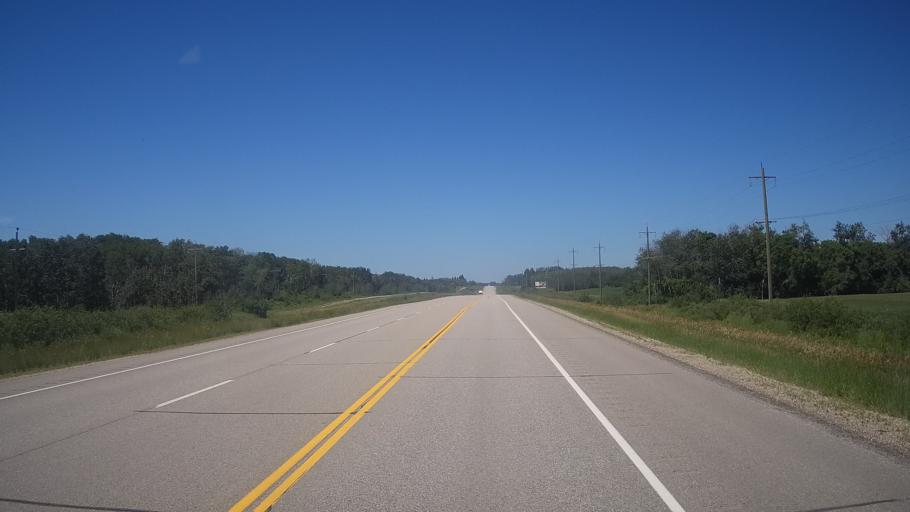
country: CA
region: Manitoba
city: Neepawa
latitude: 50.2253
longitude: -99.3485
